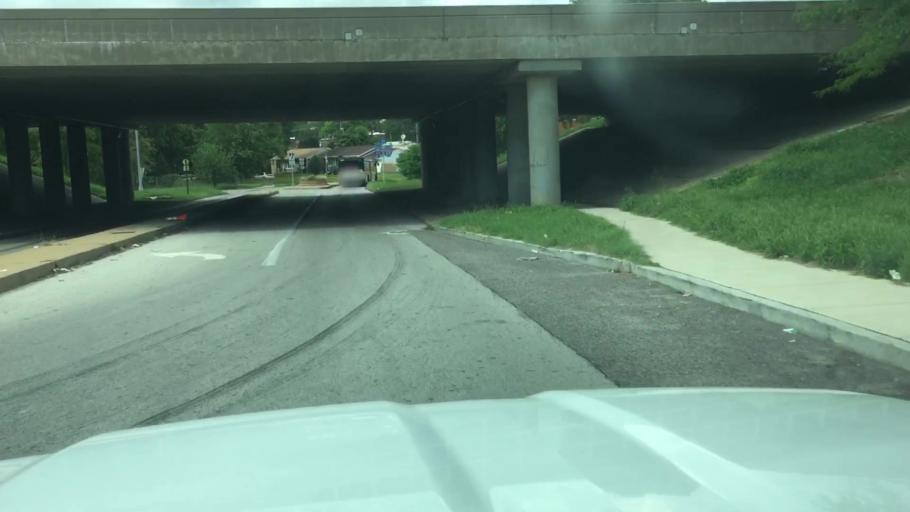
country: US
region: Missouri
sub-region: Saint Louis County
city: Lemay
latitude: 38.5625
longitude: -90.2462
